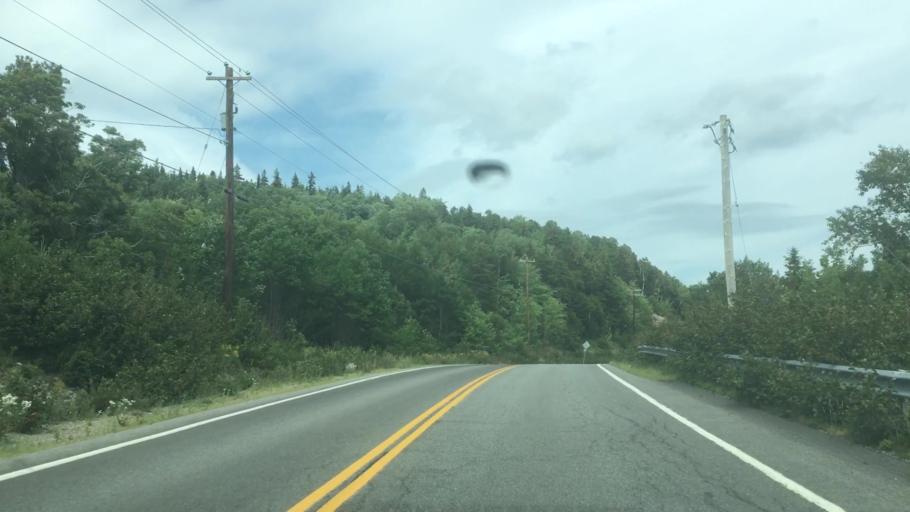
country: CA
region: Nova Scotia
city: Sydney Mines
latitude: 46.5326
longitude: -60.4172
